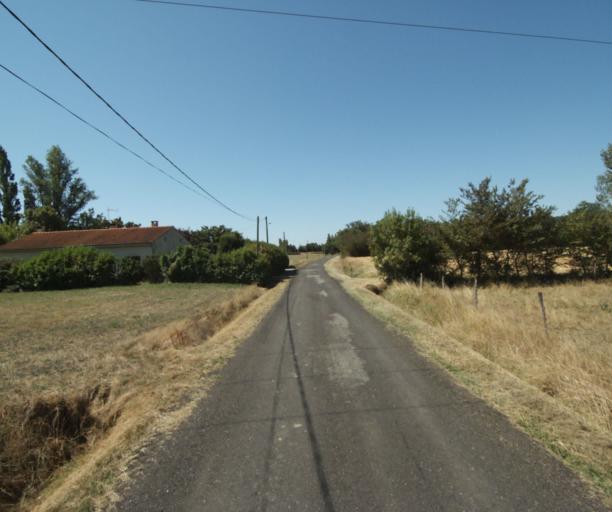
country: FR
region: Midi-Pyrenees
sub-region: Departement de la Haute-Garonne
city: Revel
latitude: 43.4700
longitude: 1.9802
